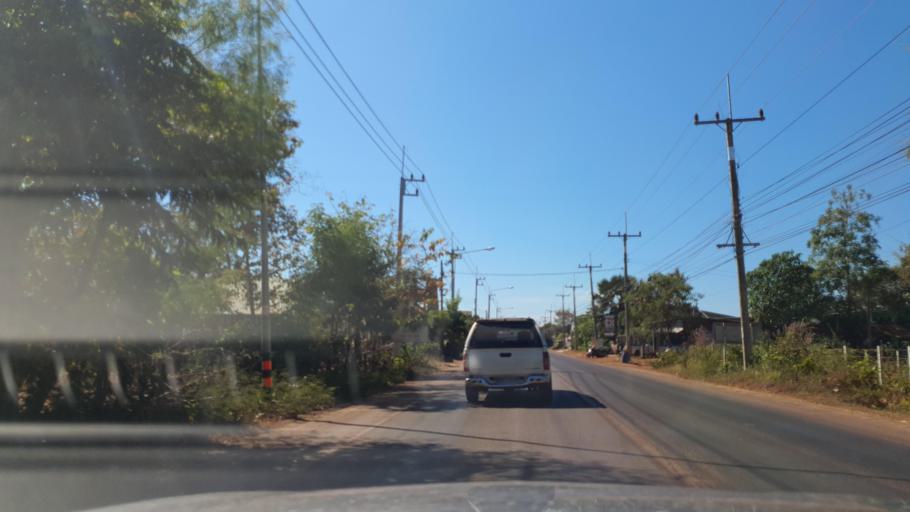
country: TH
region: Sakon Nakhon
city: Phon Na Kaeo
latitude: 17.2620
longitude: 104.1905
